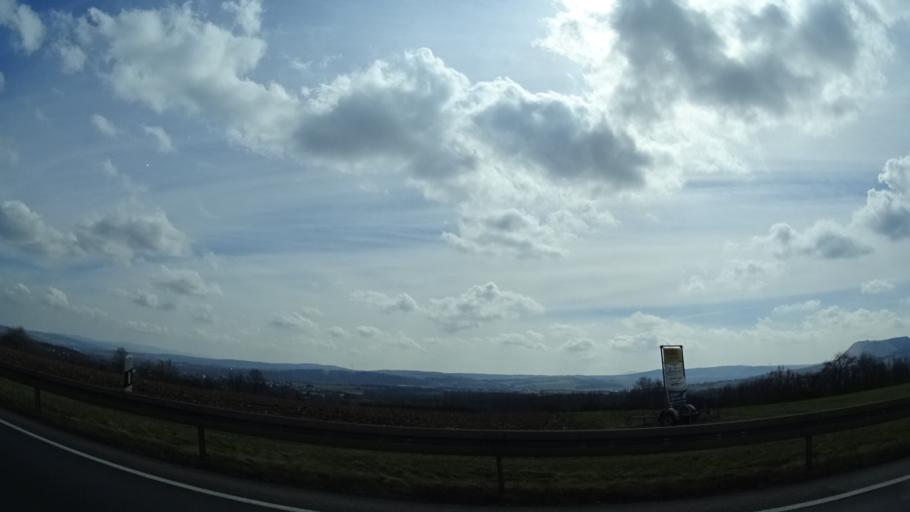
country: DE
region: Thuringia
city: Dankmarshausen
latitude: 50.9580
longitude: 10.0047
